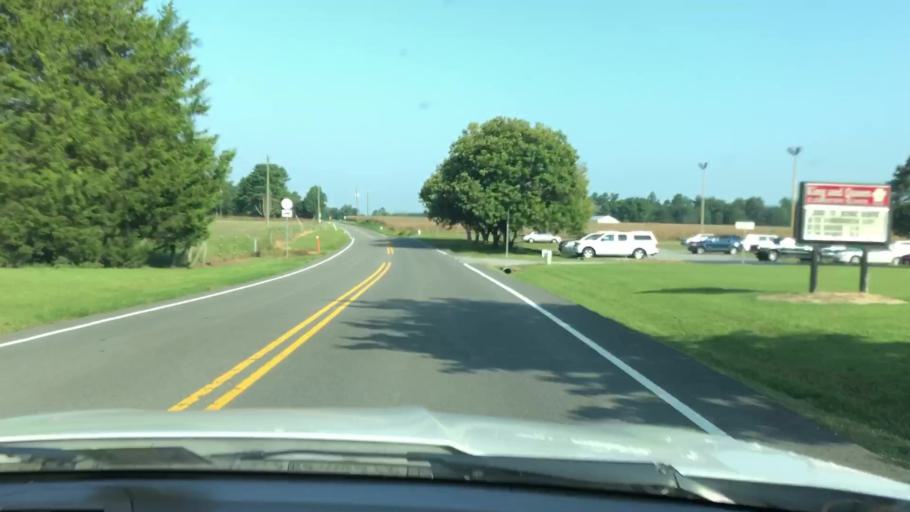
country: US
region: Virginia
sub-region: King William County
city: West Point
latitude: 37.6129
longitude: -76.7829
